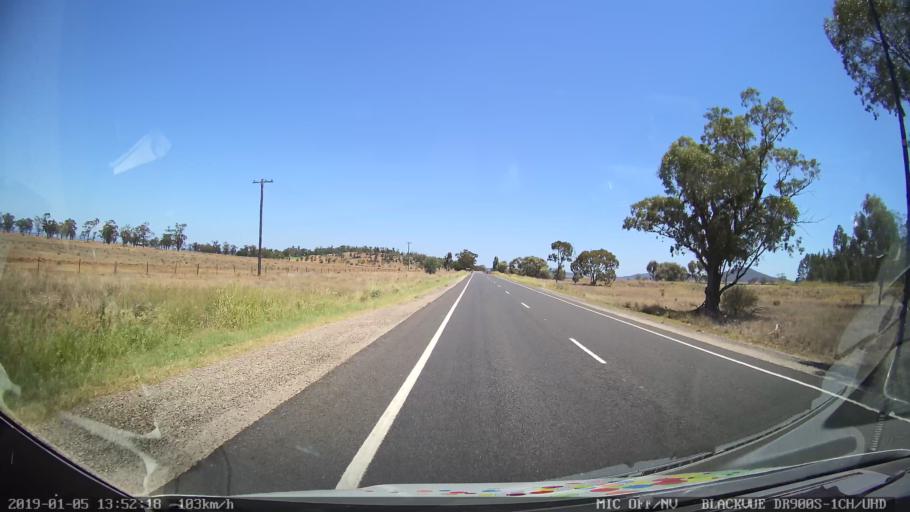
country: AU
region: New South Wales
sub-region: Gunnedah
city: Gunnedah
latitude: -31.0577
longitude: 150.2777
